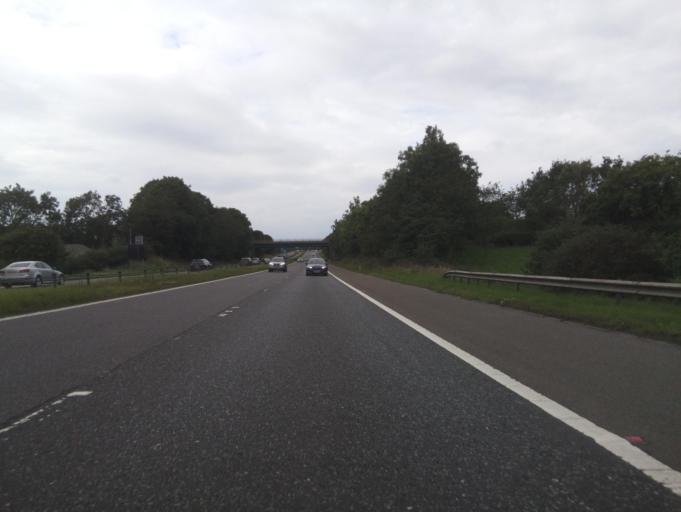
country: GB
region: England
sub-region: County Durham
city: Coxhoe
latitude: 54.7093
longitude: -1.5091
